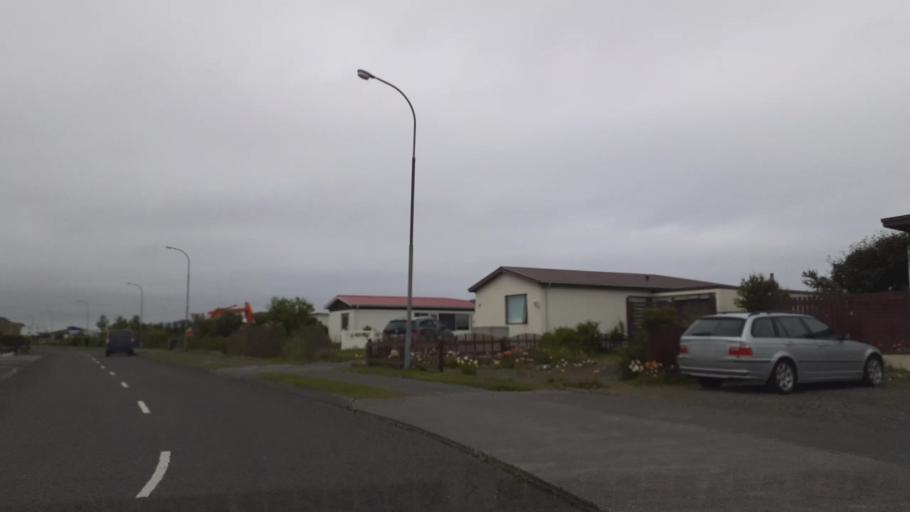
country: IS
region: Northwest
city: Saudarkrokur
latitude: 65.6586
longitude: -20.3037
